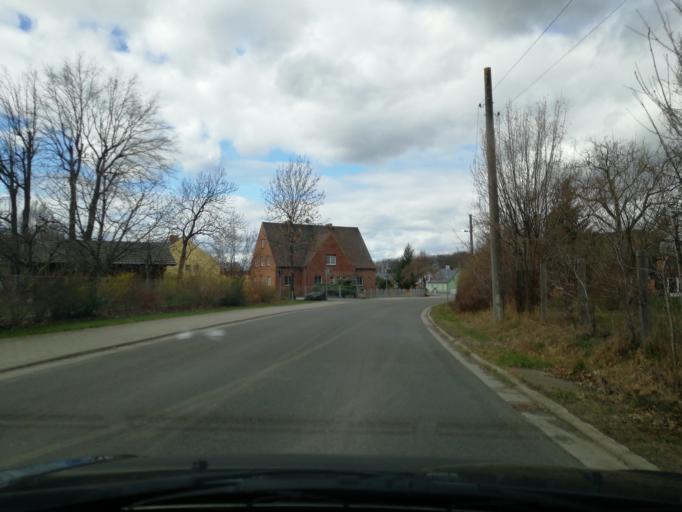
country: DE
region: Brandenburg
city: Altdobern
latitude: 51.7117
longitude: 14.0469
